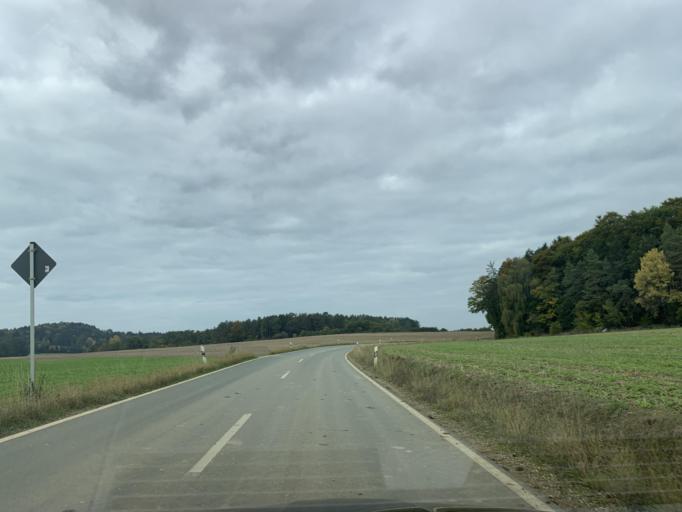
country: DE
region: Bavaria
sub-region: Upper Franconia
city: Unterleinleiter
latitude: 49.8469
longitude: 11.2390
